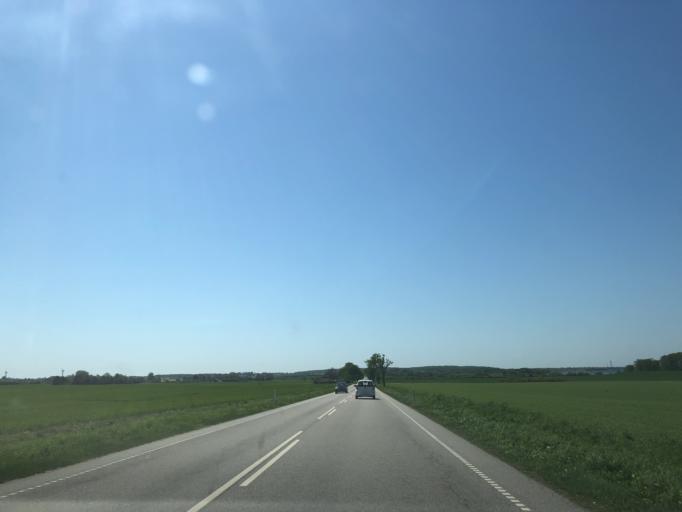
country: DK
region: Zealand
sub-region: Slagelse Kommune
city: Forlev
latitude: 55.3439
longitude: 11.2268
